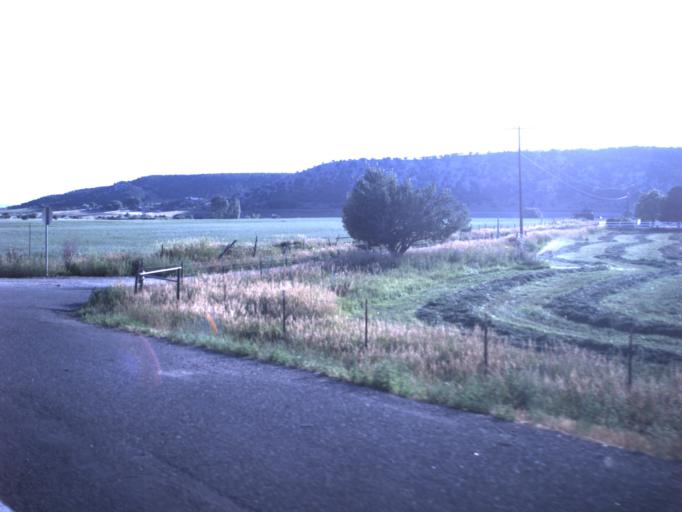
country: US
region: Utah
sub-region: Sanpete County
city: Fairview
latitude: 39.5941
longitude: -111.4464
